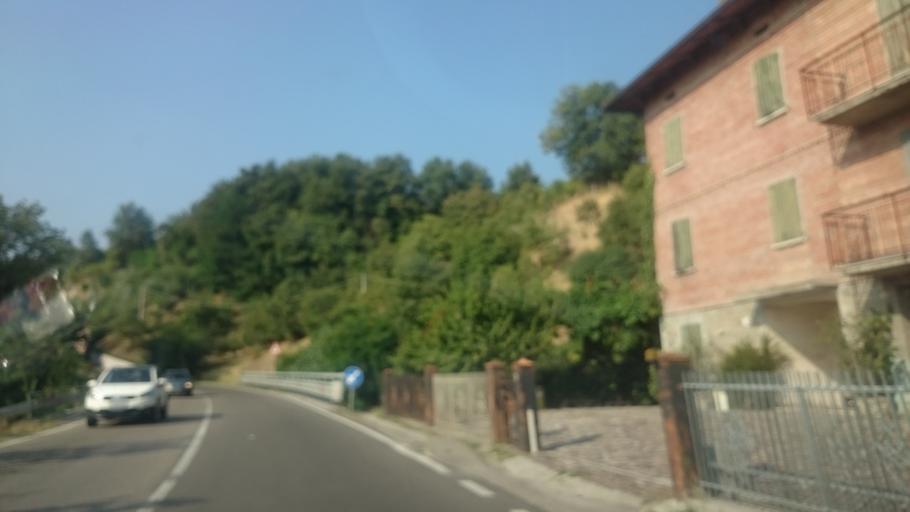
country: IT
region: Emilia-Romagna
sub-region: Provincia di Reggio Emilia
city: Castellarano
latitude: 44.4985
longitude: 10.7164
